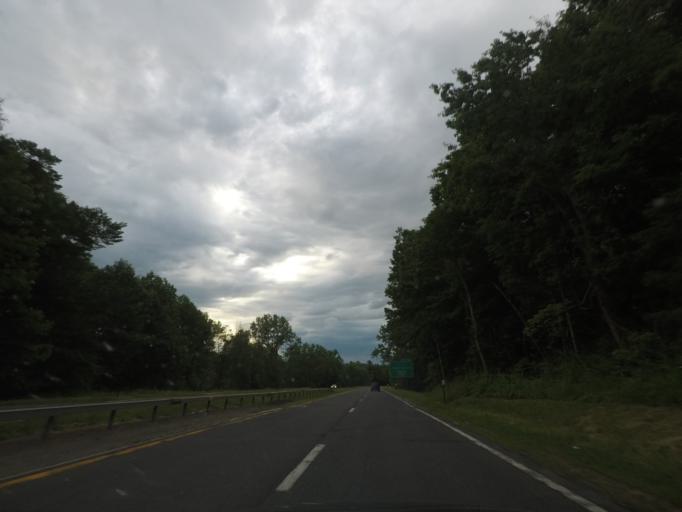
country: US
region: New York
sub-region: Dutchess County
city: Pine Plains
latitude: 42.0053
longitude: -73.7386
